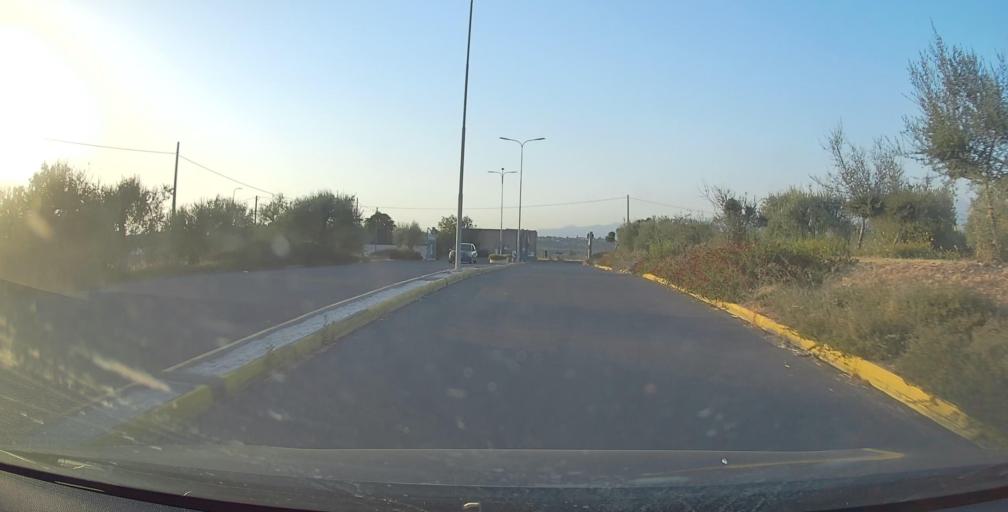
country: IT
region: Sicily
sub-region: Catania
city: Palazzolo
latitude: 37.5409
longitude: 14.9311
